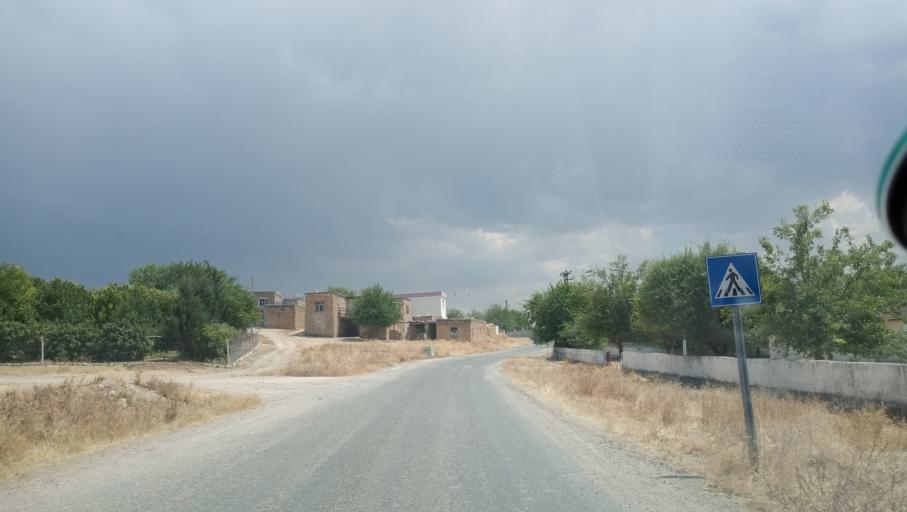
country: TR
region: Mardin
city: Baskavak
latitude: 37.6815
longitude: 40.8474
